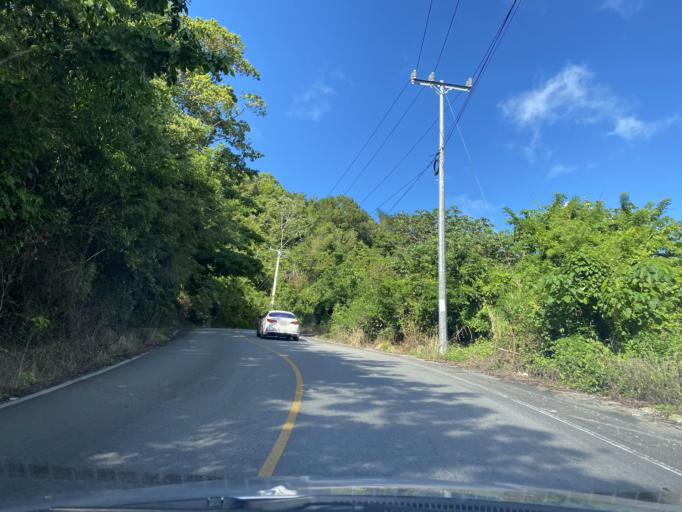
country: DO
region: Samana
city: Sanchez
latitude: 19.2401
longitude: -69.5975
